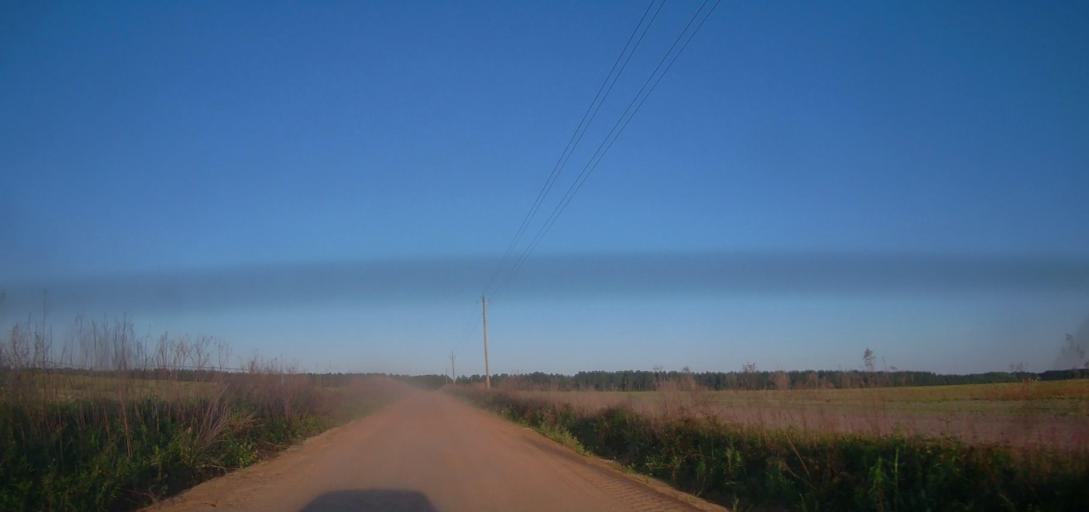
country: US
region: Georgia
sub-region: Irwin County
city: Ocilla
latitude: 31.6538
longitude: -83.2381
